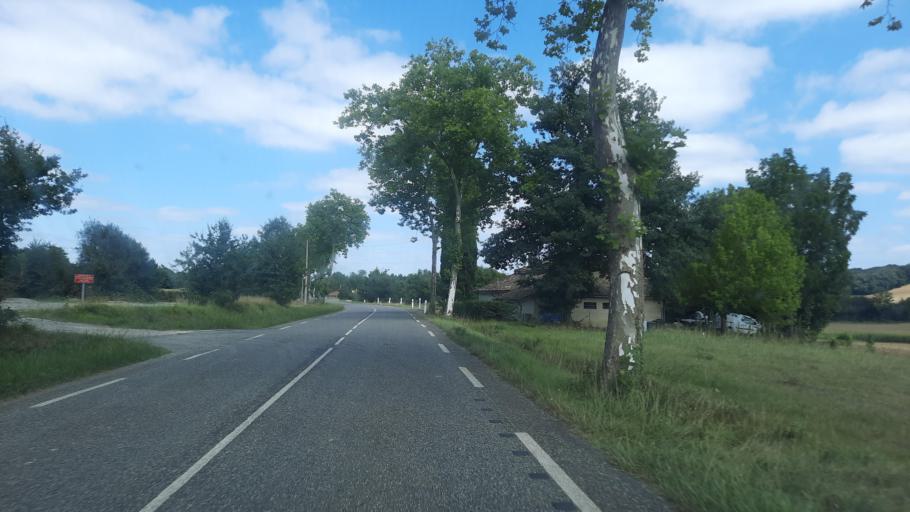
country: FR
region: Midi-Pyrenees
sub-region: Departement du Gers
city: Lombez
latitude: 43.3892
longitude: 0.7808
